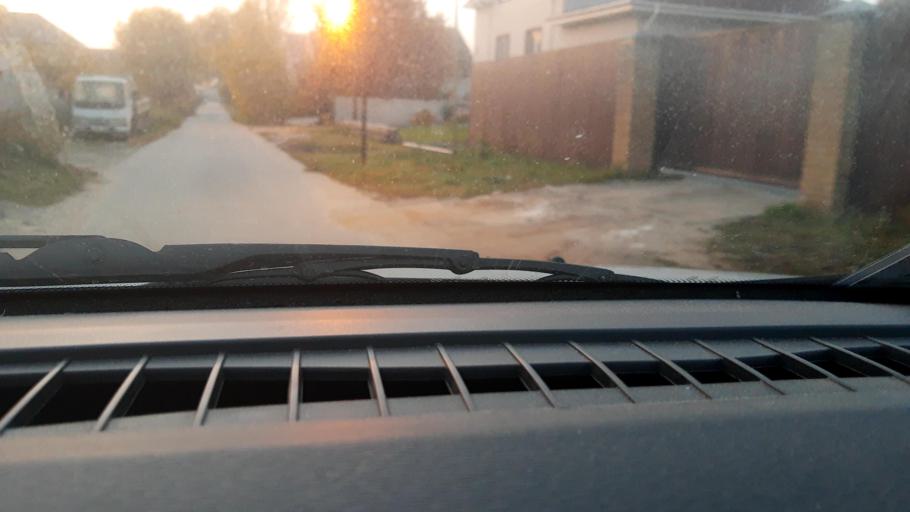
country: RU
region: Nizjnij Novgorod
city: Bor
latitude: 56.3807
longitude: 44.0353
